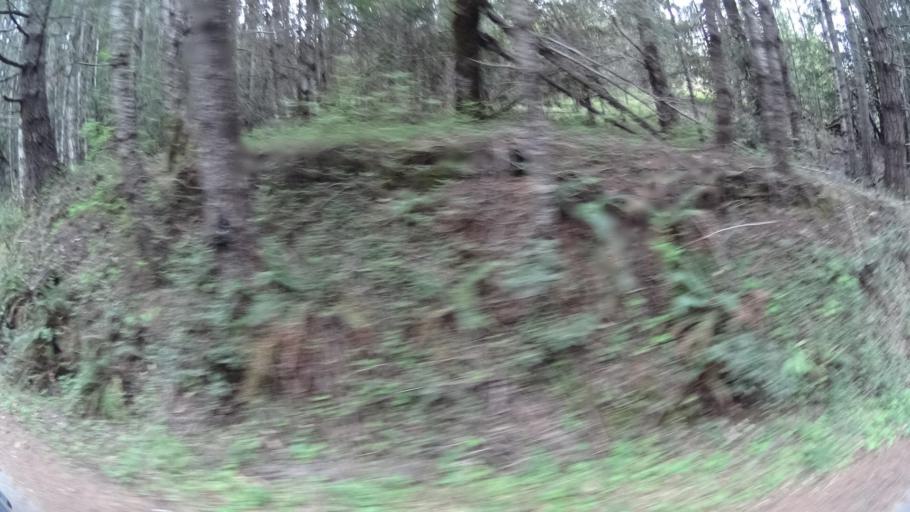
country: US
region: California
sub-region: Humboldt County
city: Redway
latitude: 40.2146
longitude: -123.7478
